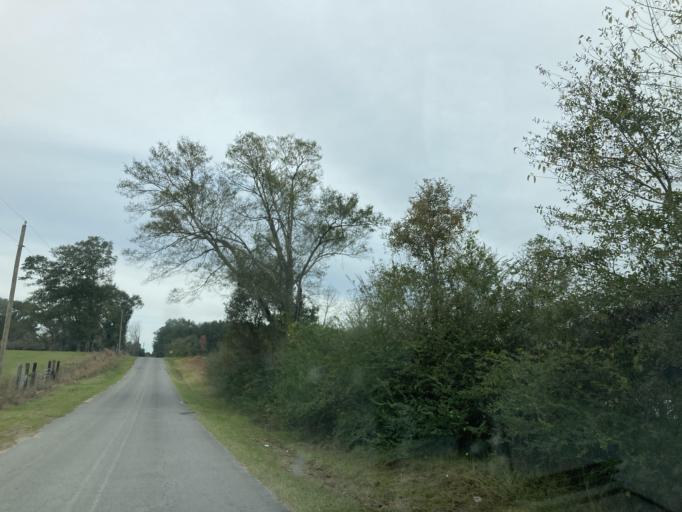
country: US
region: Mississippi
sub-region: Lamar County
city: Lumberton
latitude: 31.0479
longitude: -89.4505
